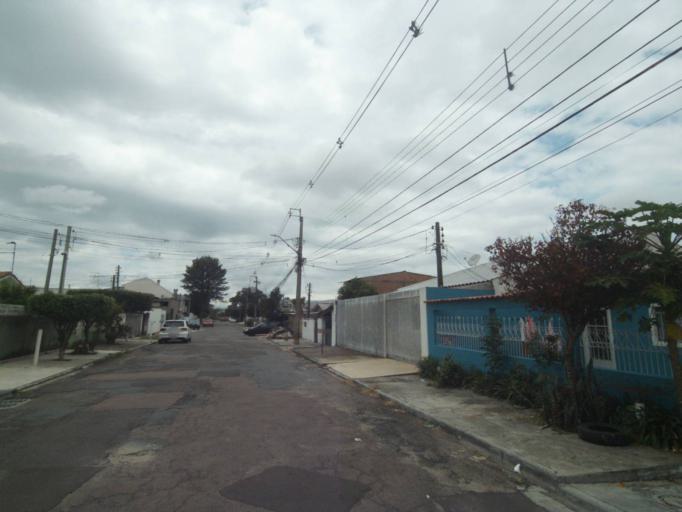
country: BR
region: Parana
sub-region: Pinhais
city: Pinhais
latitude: -25.4520
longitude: -49.2033
